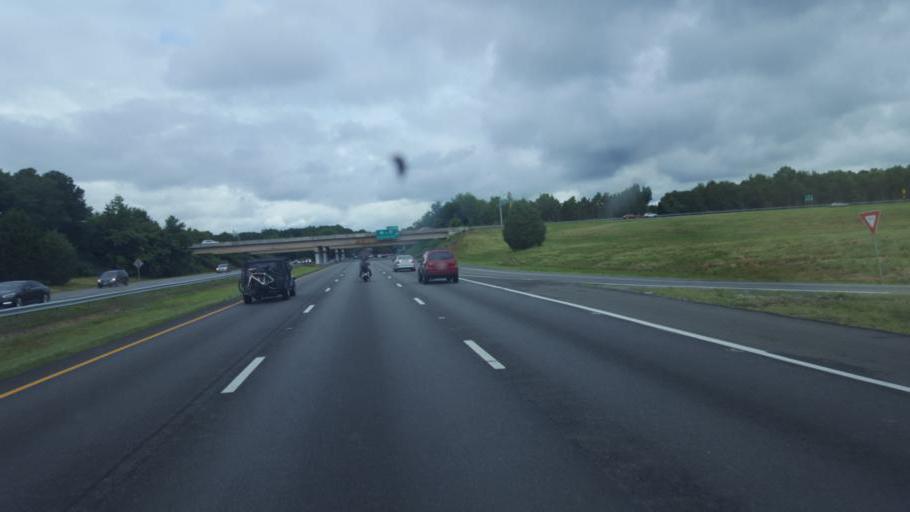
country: US
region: Virginia
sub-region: Henrico County
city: Chamberlayne
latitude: 37.6553
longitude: -77.4506
